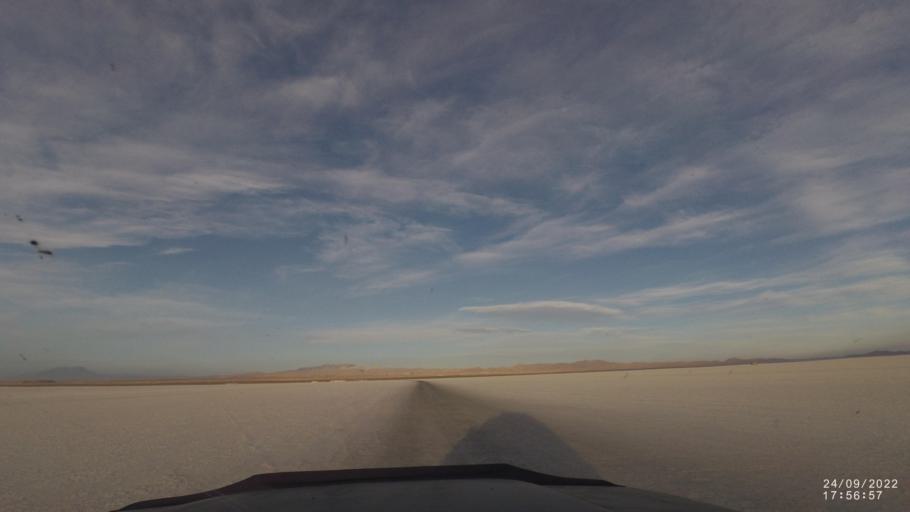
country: BO
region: Potosi
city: Colchani
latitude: -20.3225
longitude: -67.0022
